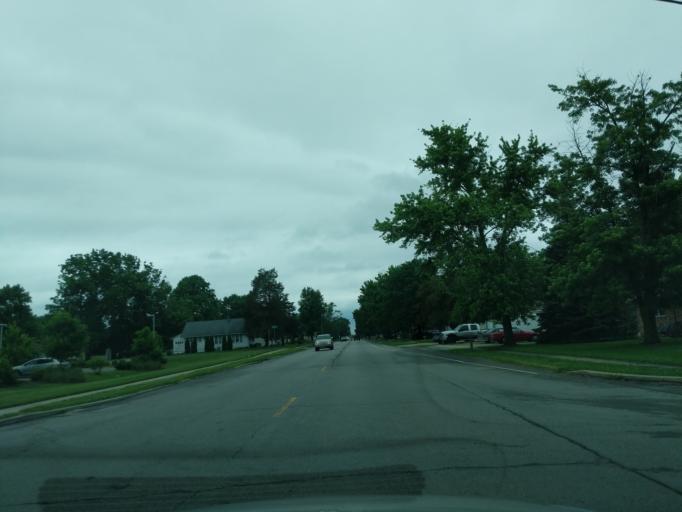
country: US
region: Indiana
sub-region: Hamilton County
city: Cicero
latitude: 40.1239
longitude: -86.0135
